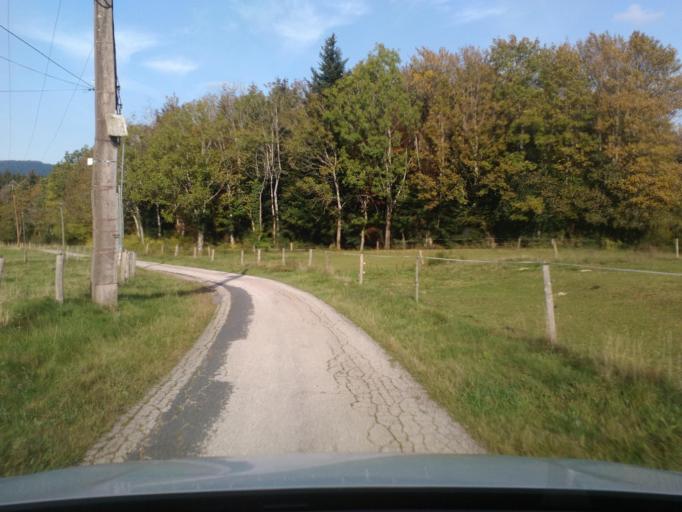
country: FR
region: Lorraine
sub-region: Departement des Vosges
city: Senones
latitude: 48.4040
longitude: 7.0754
